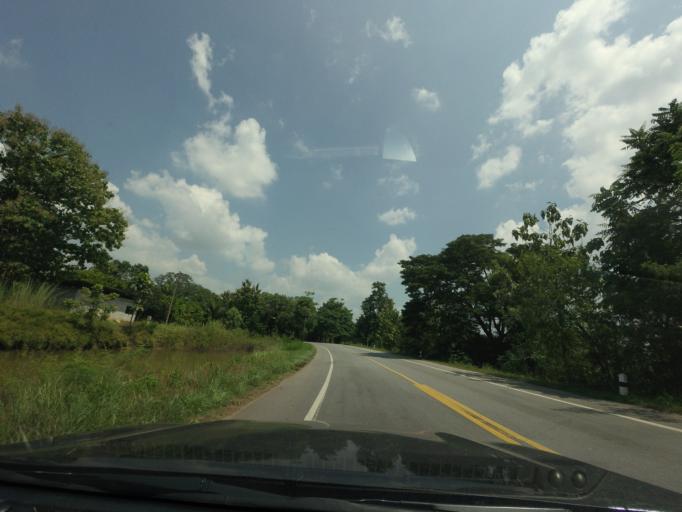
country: TH
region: Phitsanulok
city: Chat Trakan
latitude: 17.2966
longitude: 100.4116
